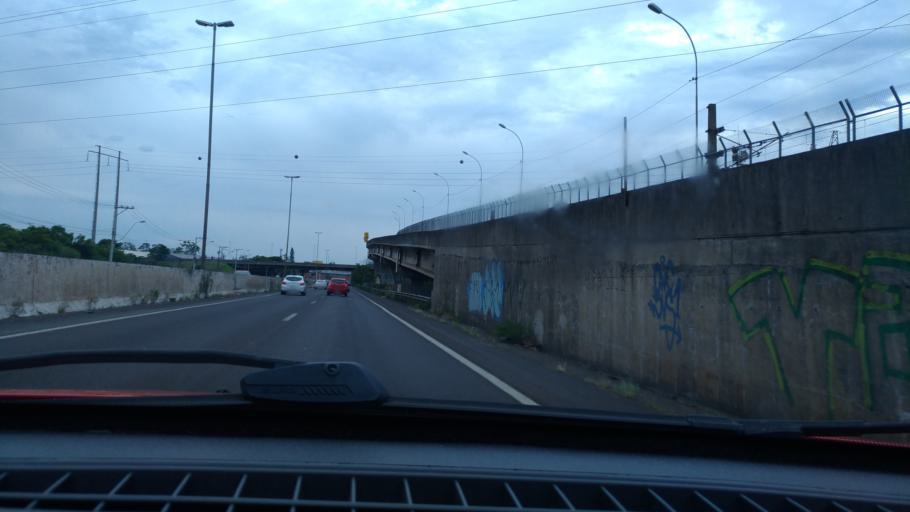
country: BR
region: Rio Grande do Sul
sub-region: Canoas
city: Canoas
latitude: -29.8898
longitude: -51.1785
